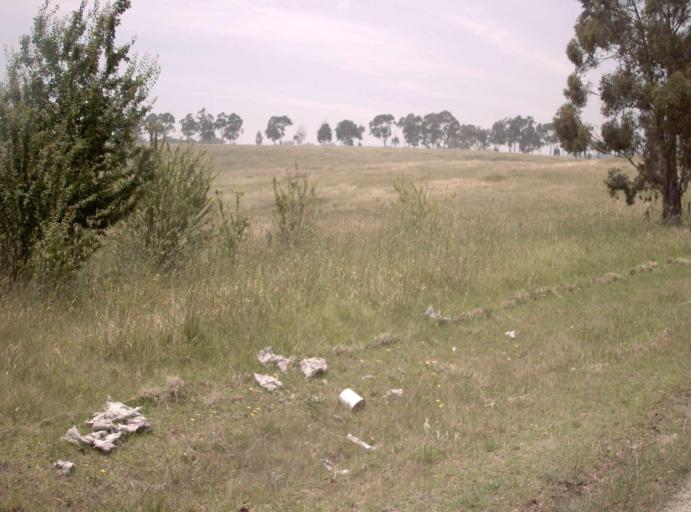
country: AU
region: Victoria
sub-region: Latrobe
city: Traralgon
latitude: -38.2479
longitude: 146.6518
